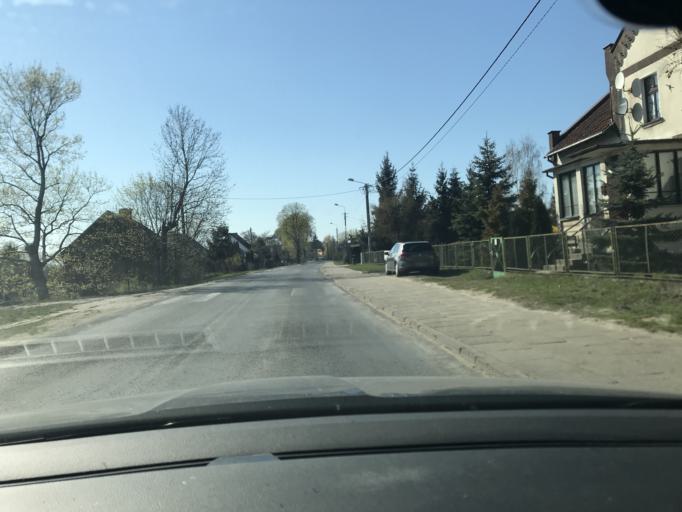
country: PL
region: Pomeranian Voivodeship
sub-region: Powiat nowodworski
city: Sztutowo
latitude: 54.3263
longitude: 19.1687
